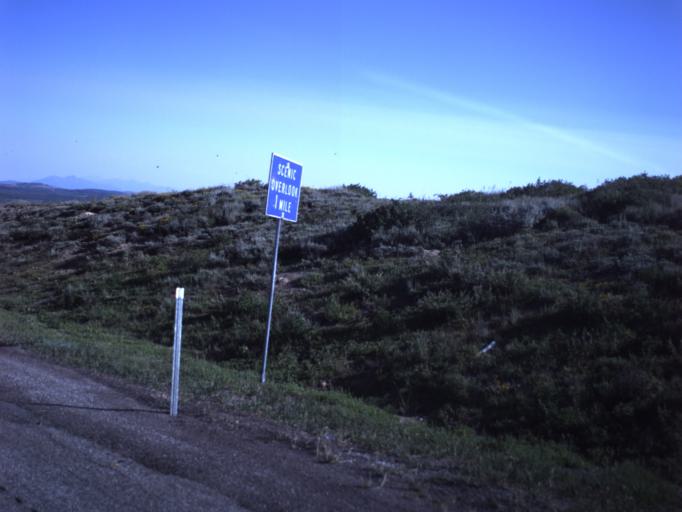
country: US
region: Utah
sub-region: Sanpete County
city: Fairview
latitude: 39.6199
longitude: -111.3125
